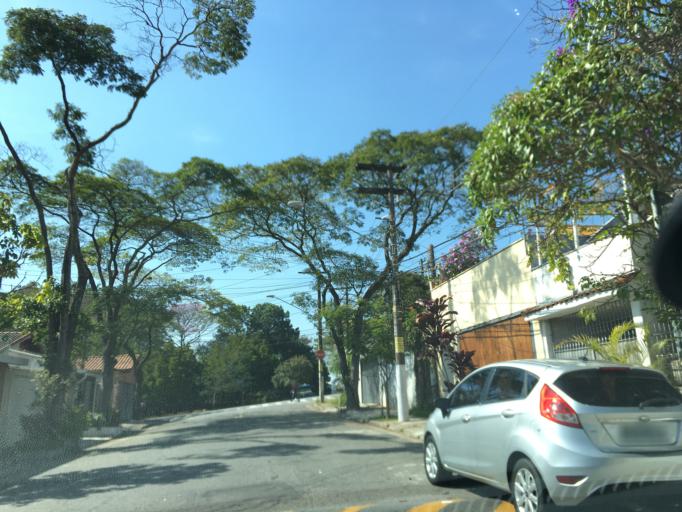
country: BR
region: Sao Paulo
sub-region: Osasco
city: Osasco
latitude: -23.5761
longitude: -46.7261
